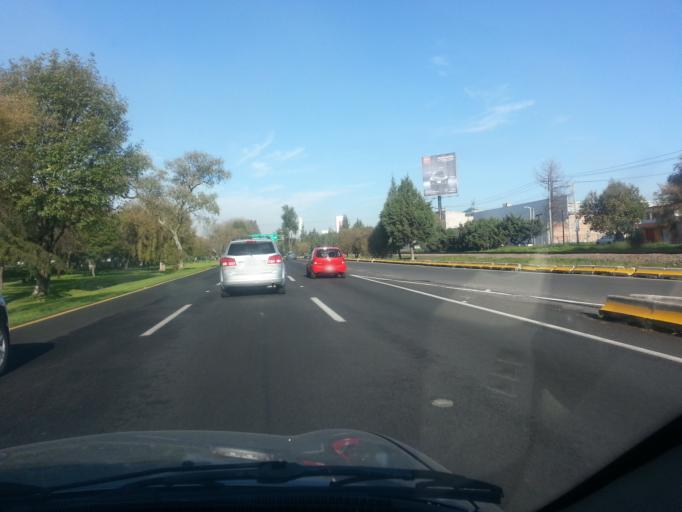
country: MX
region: Mexico
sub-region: San Mateo Atenco
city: Santa Maria la Asuncion
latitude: 19.2866
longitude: -99.5630
